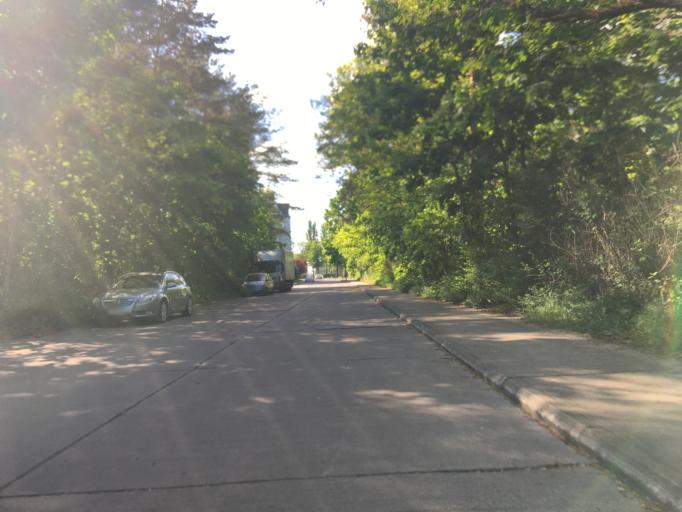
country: DE
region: Berlin
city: Adlershof
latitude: 52.4527
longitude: 13.5514
